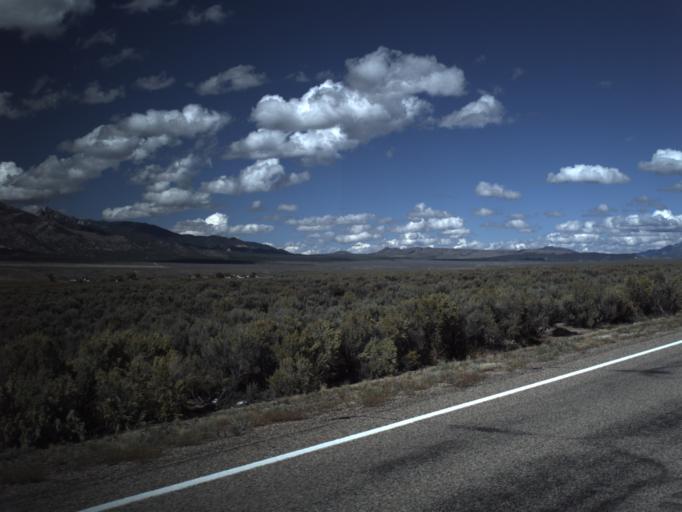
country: US
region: Utah
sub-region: Beaver County
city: Beaver
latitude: 38.2319
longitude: -112.7995
